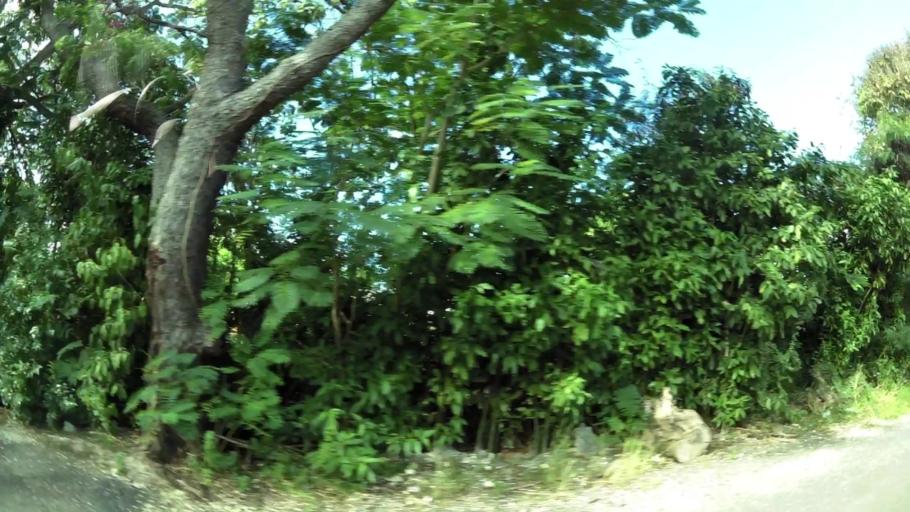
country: GP
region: Guadeloupe
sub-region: Guadeloupe
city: Port-Louis
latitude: 16.4169
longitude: -61.5268
